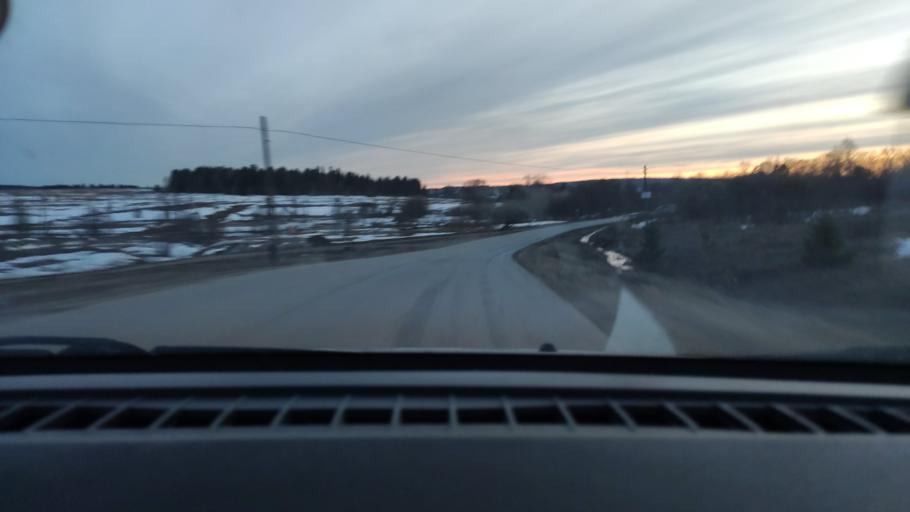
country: RU
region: Perm
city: Yug
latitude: 57.7302
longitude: 56.2066
